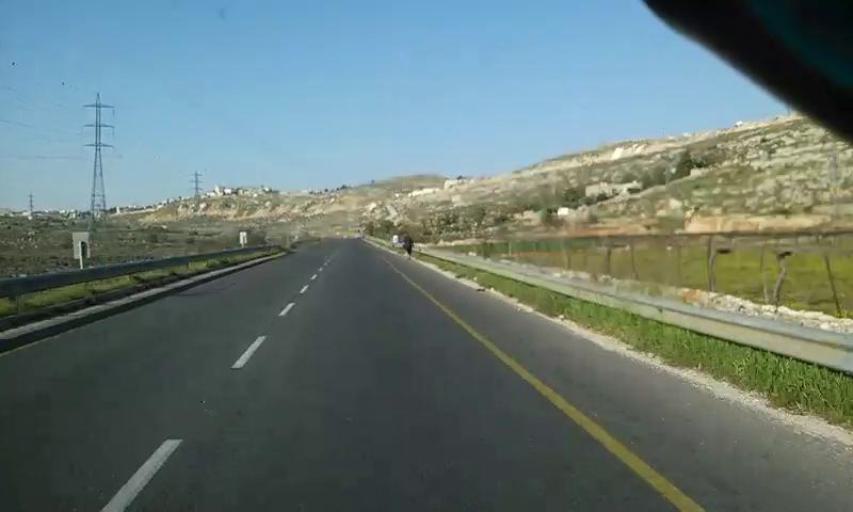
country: PS
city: Al Buq`ah
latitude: 31.5513
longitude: 35.1350
